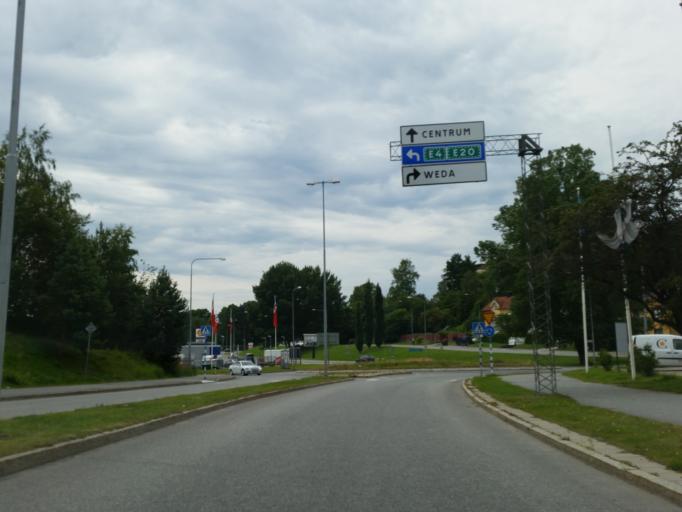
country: SE
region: Stockholm
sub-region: Sodertalje Kommun
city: Soedertaelje
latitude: 59.2046
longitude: 17.6456
